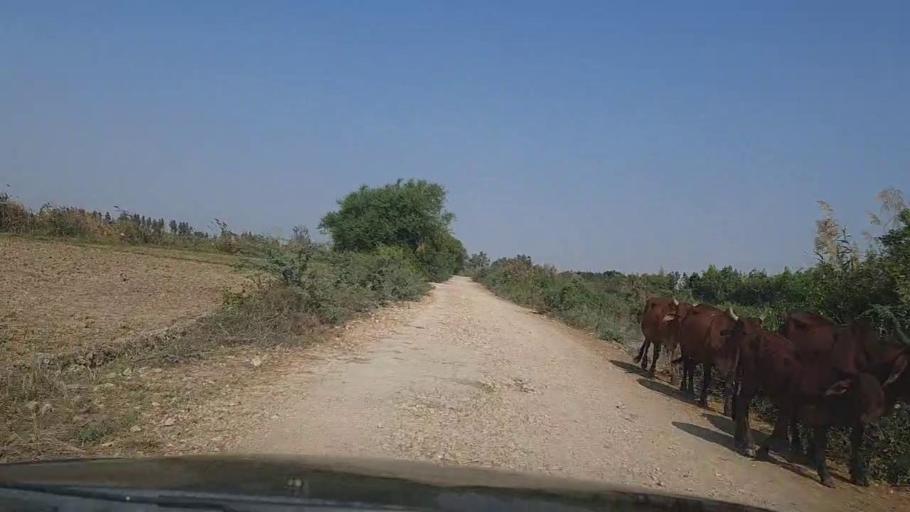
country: PK
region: Sindh
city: Thatta
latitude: 24.6309
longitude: 67.8135
